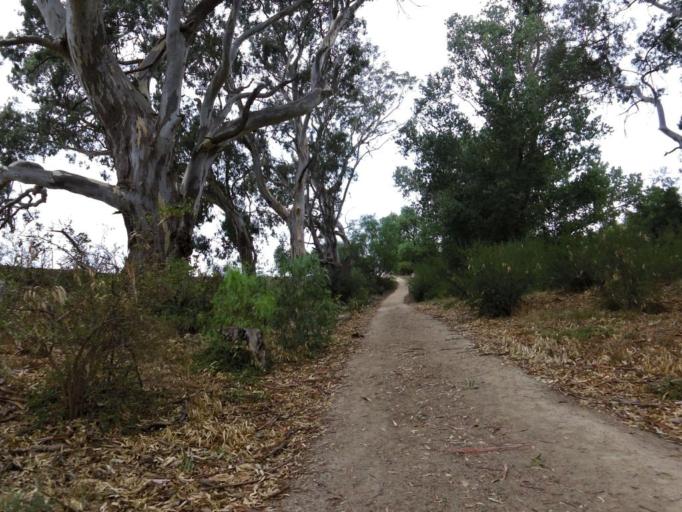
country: AU
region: Victoria
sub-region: Moorabool
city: Bacchus Marsh
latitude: -37.6578
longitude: 144.4503
